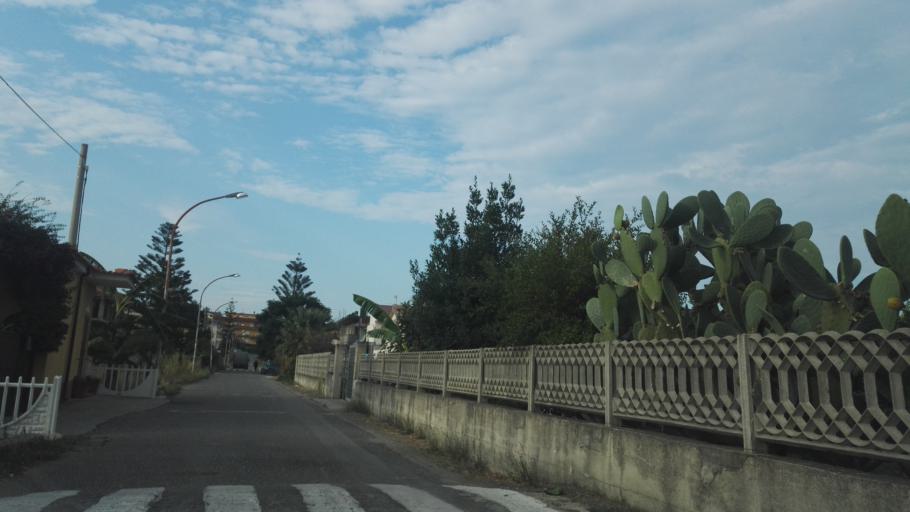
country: IT
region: Calabria
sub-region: Provincia di Reggio Calabria
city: Monasterace Marina
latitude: 38.4317
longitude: 16.5694
